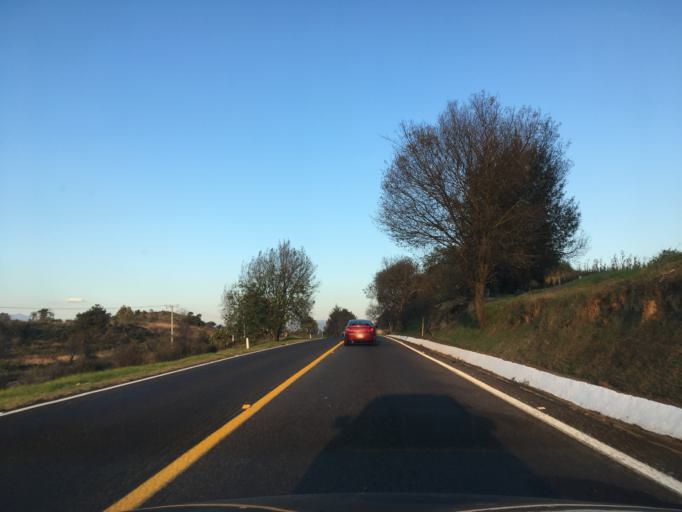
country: MX
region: Michoacan
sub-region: Patzcuaro
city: Santa Ana Chapitiro
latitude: 19.5300
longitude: -101.6393
